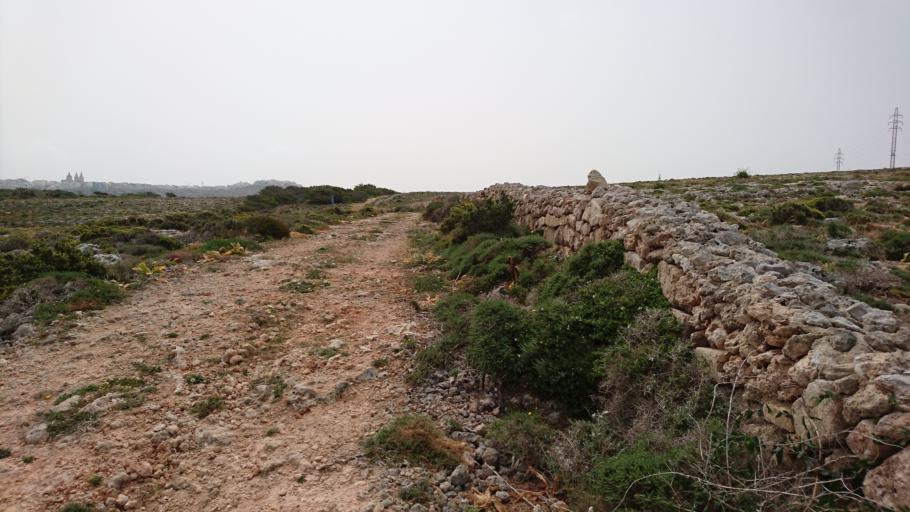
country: MT
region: Il-Mellieha
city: Mellieha
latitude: 35.9679
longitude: 14.3431
